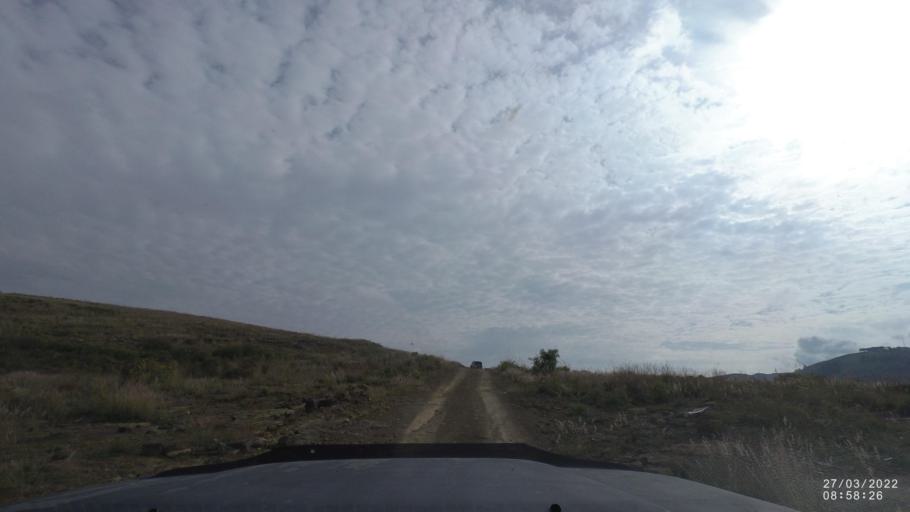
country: BO
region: Cochabamba
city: Cliza
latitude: -17.7427
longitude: -65.8569
